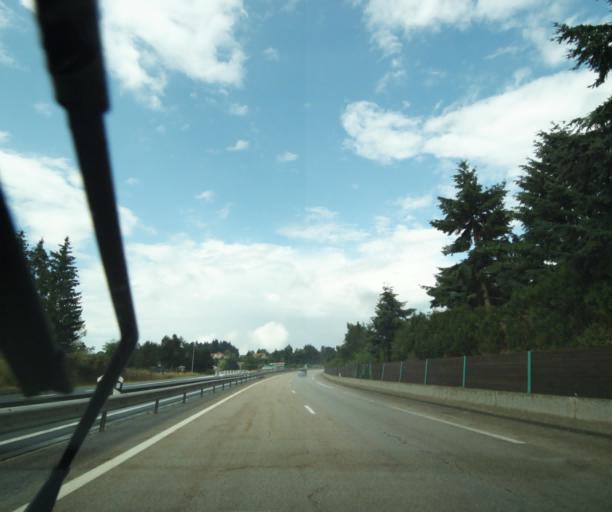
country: FR
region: Auvergne
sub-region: Departement de la Haute-Loire
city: Saint-Maurice-de-Lignon
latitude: 45.2286
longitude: 4.1370
